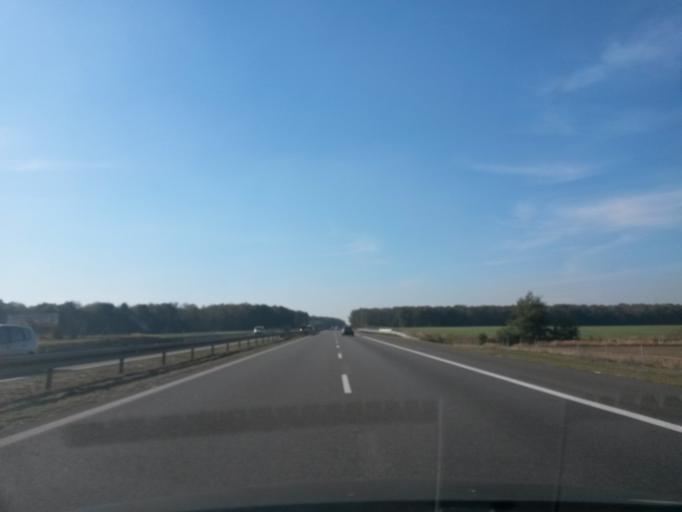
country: PL
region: Opole Voivodeship
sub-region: Powiat strzelecki
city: Strzelce Opolskie
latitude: 50.4512
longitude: 18.3140
